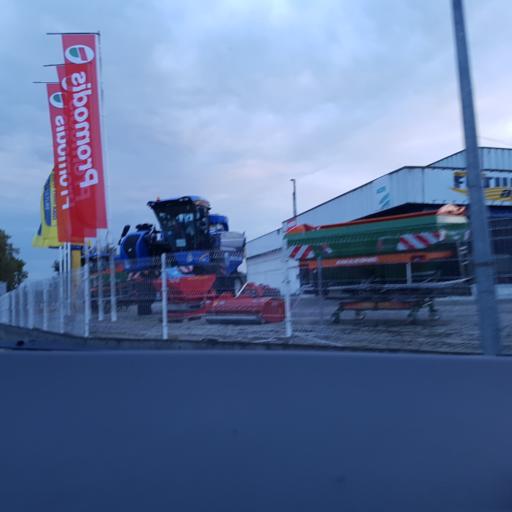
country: FR
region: Midi-Pyrenees
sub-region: Departement du Gers
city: Condom
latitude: 43.9462
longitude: 0.3616
